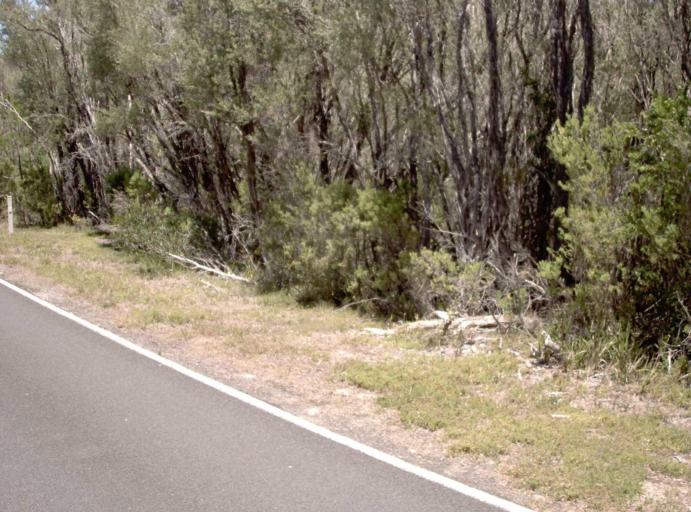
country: AU
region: Victoria
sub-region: Latrobe
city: Morwell
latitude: -38.8703
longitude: 146.2649
